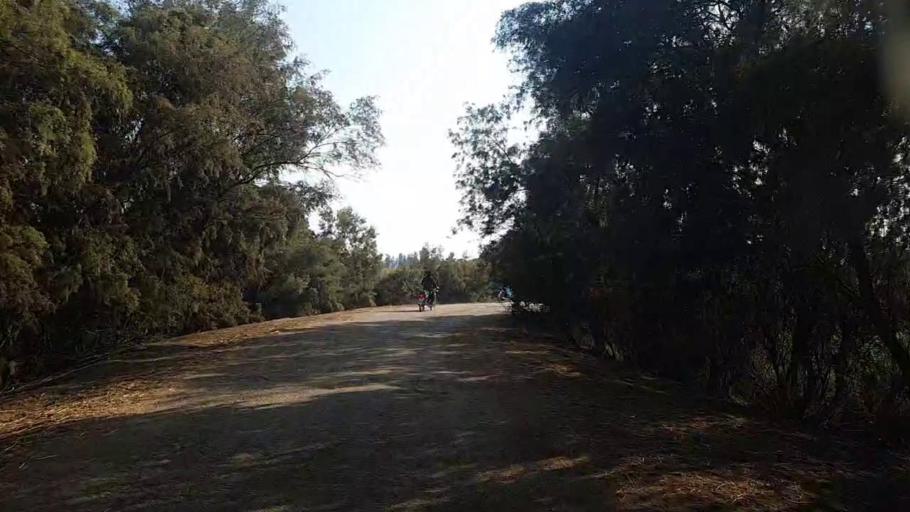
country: PK
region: Sindh
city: Mirpur Mathelo
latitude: 27.8964
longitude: 69.6070
